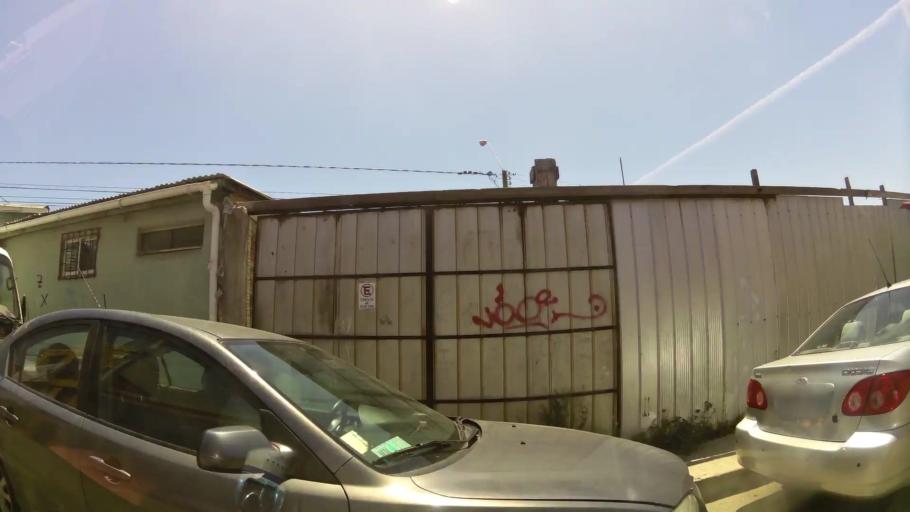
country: CL
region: Valparaiso
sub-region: Provincia de Valparaiso
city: Valparaiso
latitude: -33.0339
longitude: -71.6380
